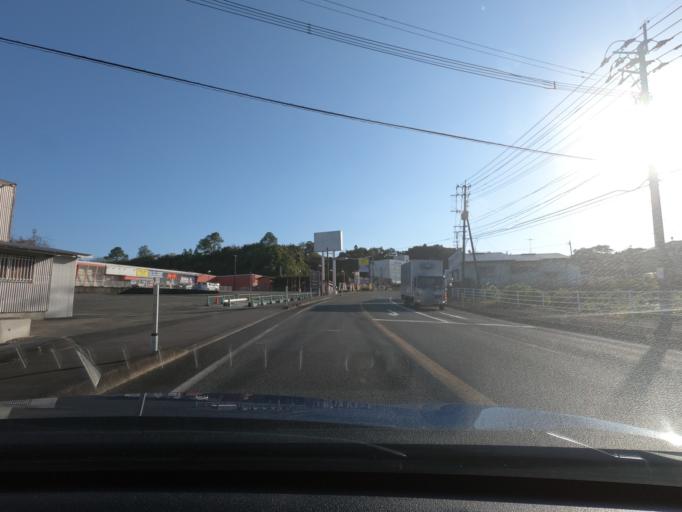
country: JP
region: Kagoshima
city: Akune
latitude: 32.0408
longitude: 130.2162
